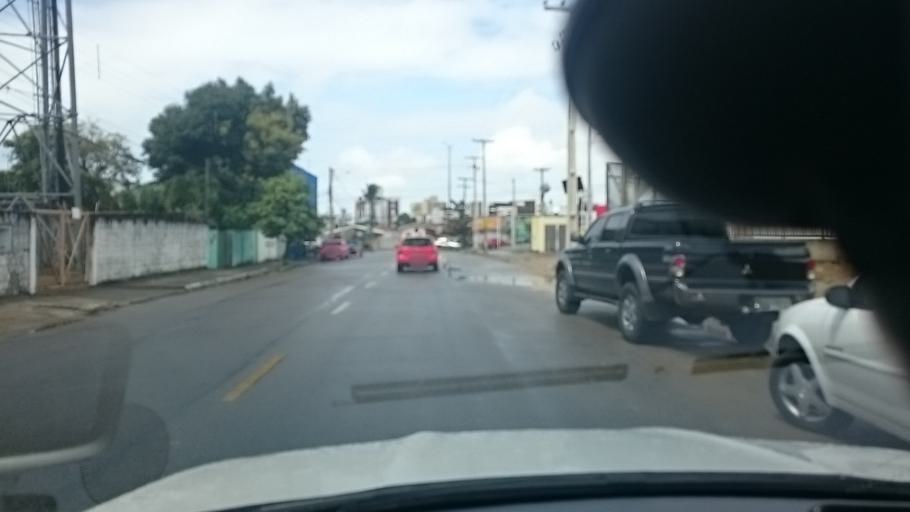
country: BR
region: Paraiba
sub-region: Joao Pessoa
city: Joao Pessoa
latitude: -7.1486
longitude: -34.8413
